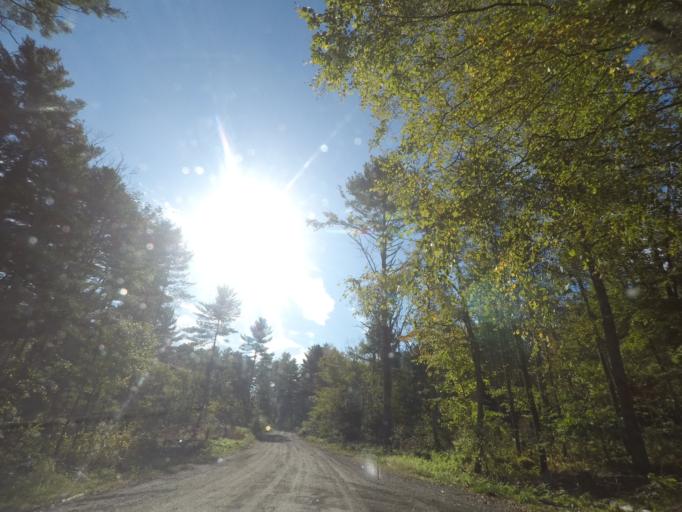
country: US
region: Connecticut
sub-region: Windham County
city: Thompson
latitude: 41.9717
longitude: -71.8208
